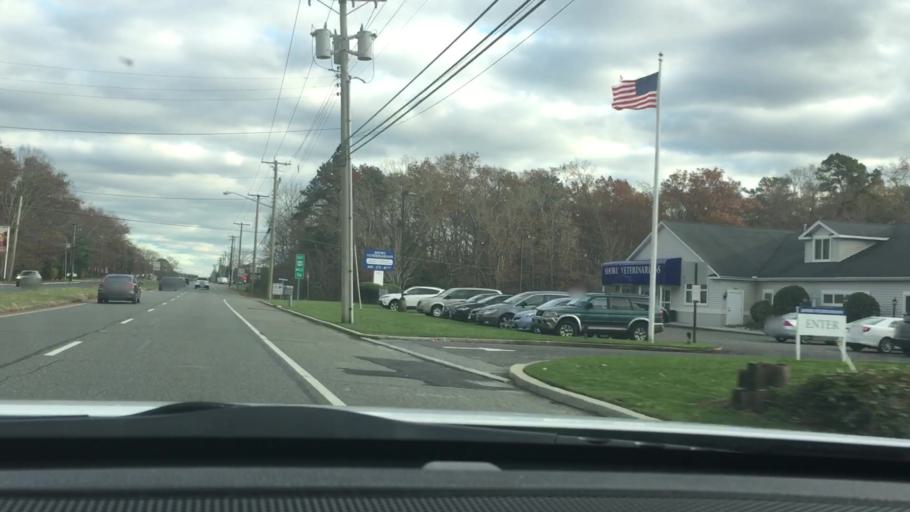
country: US
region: New Jersey
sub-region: Atlantic County
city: Northfield
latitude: 39.4154
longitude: -74.5776
